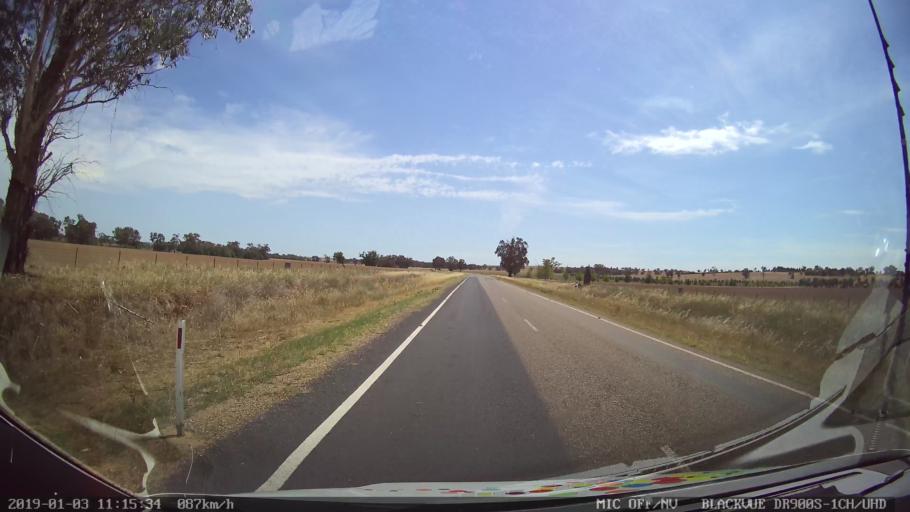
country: AU
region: New South Wales
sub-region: Young
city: Young
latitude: -34.1624
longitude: 148.2658
